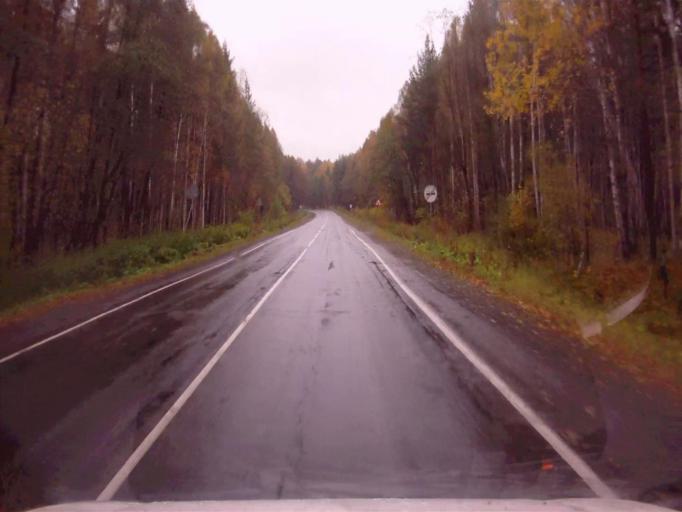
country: RU
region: Chelyabinsk
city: Verkhniy Ufaley
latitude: 55.9554
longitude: 60.3914
